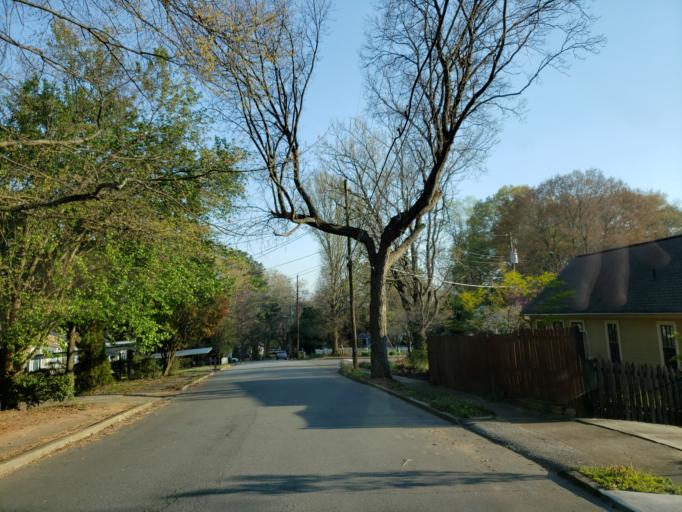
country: US
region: Georgia
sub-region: Cobb County
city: Marietta
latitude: 33.9485
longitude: -84.5277
